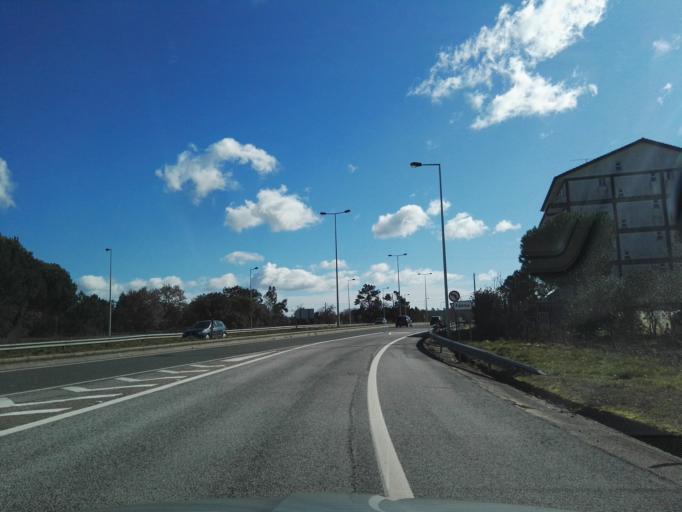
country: PT
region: Santarem
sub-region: Ourem
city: Fatima
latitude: 39.6296
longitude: -8.6826
